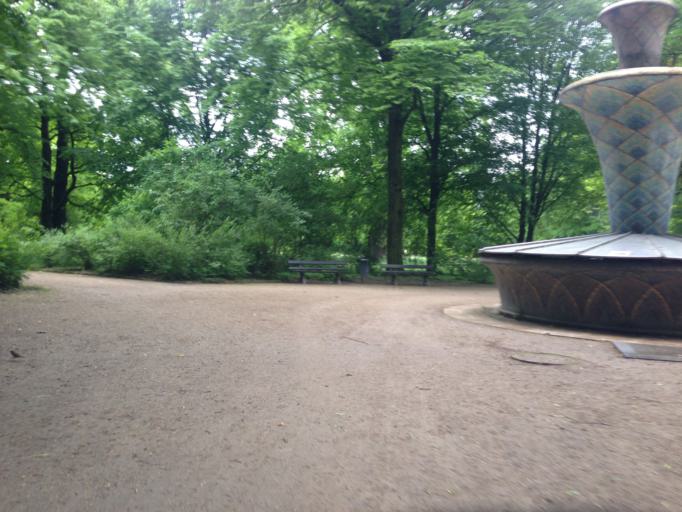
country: DE
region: Saxony
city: Dresden
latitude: 51.0407
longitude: 13.7541
